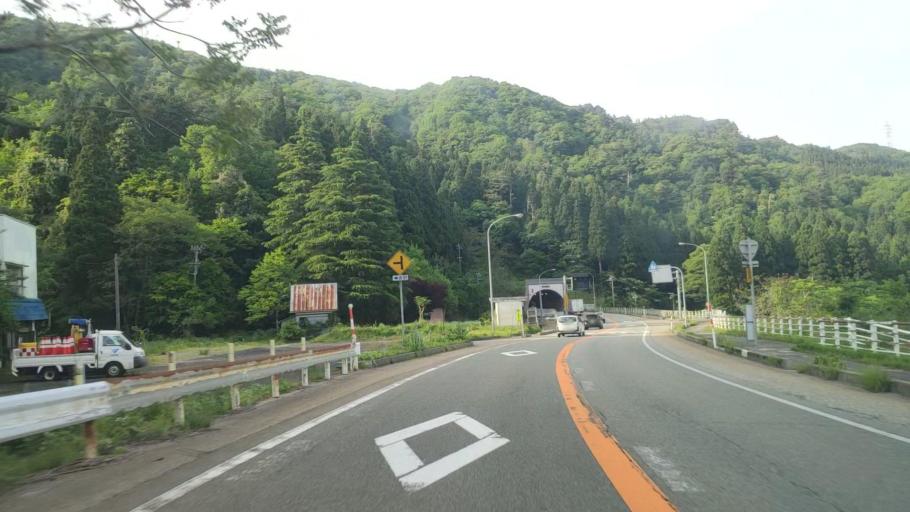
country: JP
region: Toyama
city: Yatsuomachi-higashikumisaka
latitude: 36.4947
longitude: 137.2358
